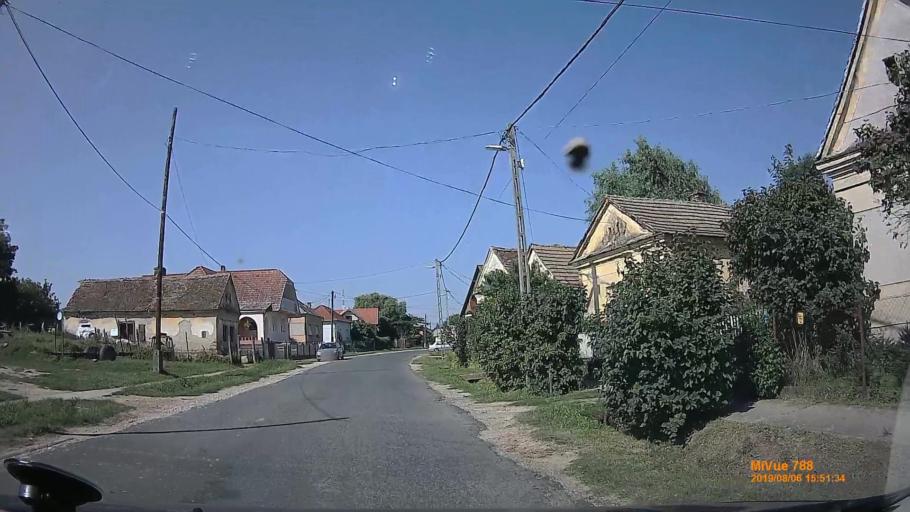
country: HU
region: Somogy
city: Csurgo
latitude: 46.2785
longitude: 17.0407
